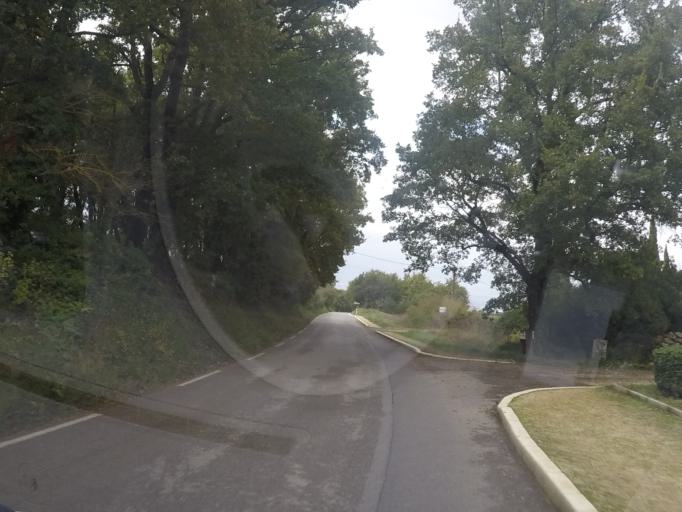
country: FR
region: Provence-Alpes-Cote d'Azur
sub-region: Departement du Vaucluse
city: Ansouis
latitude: 43.7411
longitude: 5.4586
